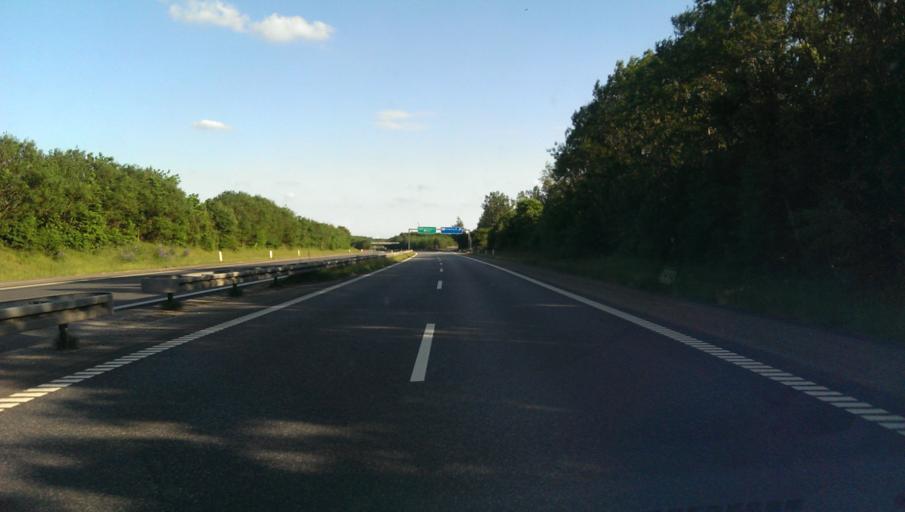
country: DK
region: South Denmark
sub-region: Esbjerg Kommune
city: Esbjerg
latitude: 55.4896
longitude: 8.5034
